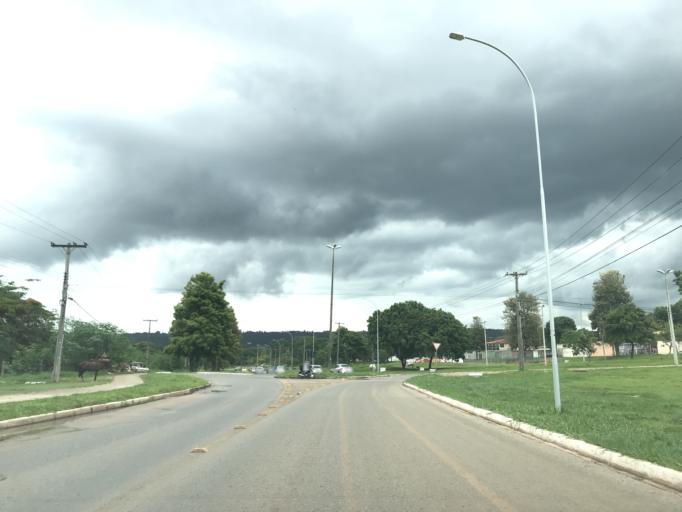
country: BR
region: Federal District
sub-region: Brasilia
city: Brasilia
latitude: -15.6465
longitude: -47.8116
